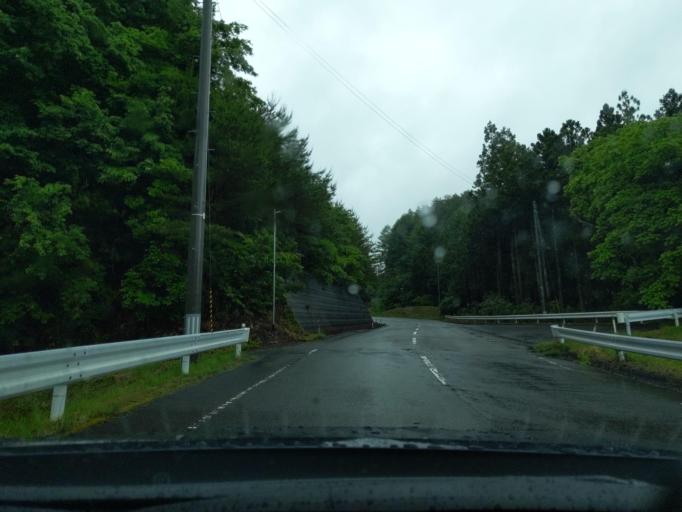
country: JP
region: Fukushima
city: Funehikimachi-funehiki
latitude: 37.5948
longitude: 140.6145
